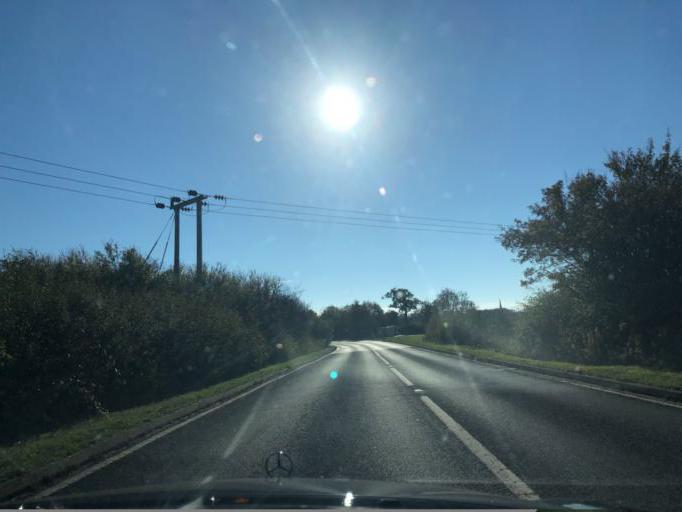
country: GB
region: England
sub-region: Warwickshire
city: Southam
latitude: 52.2349
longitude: -1.3907
